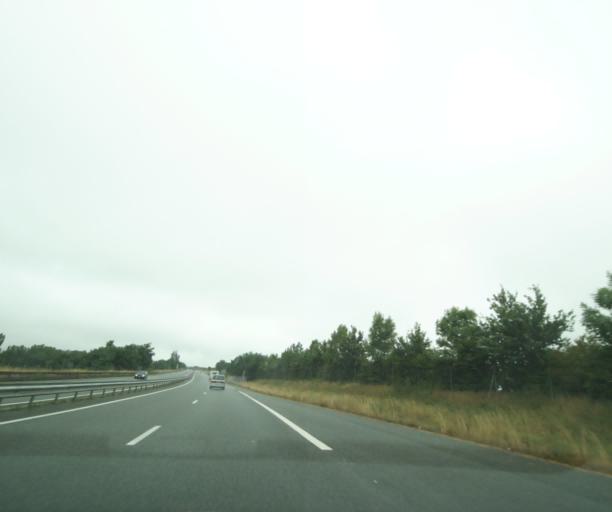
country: FR
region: Midi-Pyrenees
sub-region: Departement de l'Aveyron
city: Naucelle
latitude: 44.1052
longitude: 2.3102
